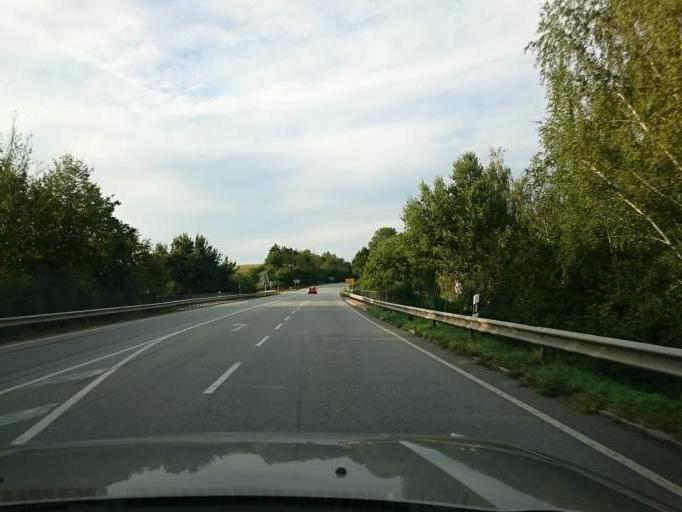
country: DE
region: Bavaria
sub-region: Lower Bavaria
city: Simbach
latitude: 48.5672
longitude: 12.7283
